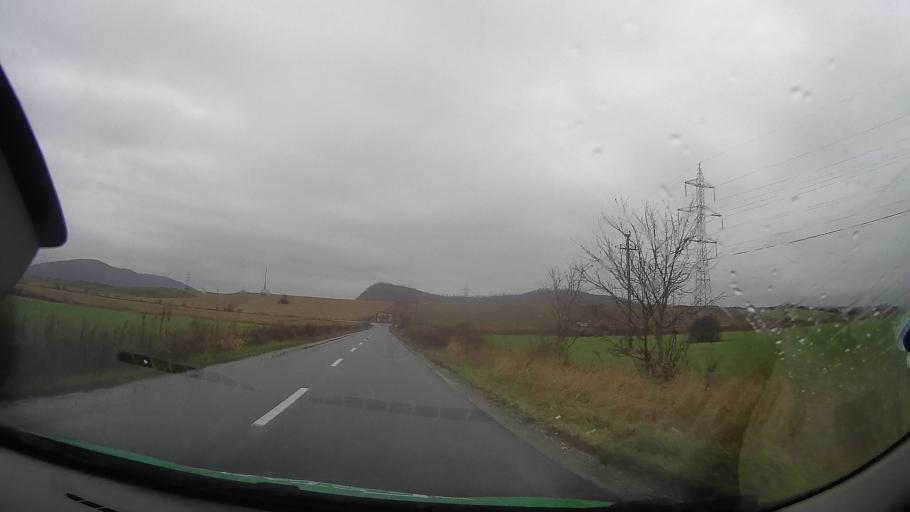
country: RO
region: Bistrita-Nasaud
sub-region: Municipiul Bistrita
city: Viisoara
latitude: 47.0545
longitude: 24.4502
